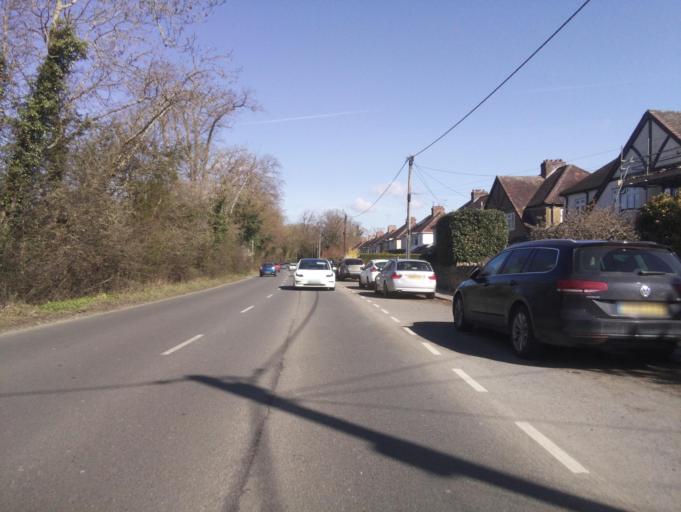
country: GB
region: England
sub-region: Wiltshire
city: Bradford-on-Avon
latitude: 51.3548
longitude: -2.2534
